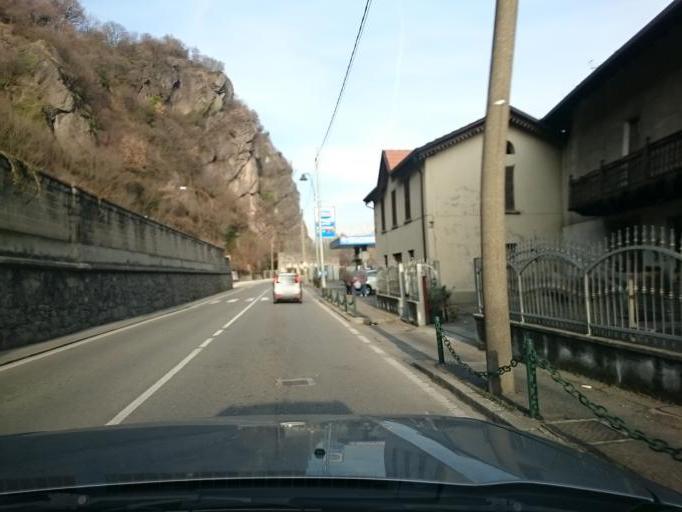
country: IT
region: Lombardy
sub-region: Provincia di Brescia
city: Darfo
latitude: 45.8866
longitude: 10.1815
